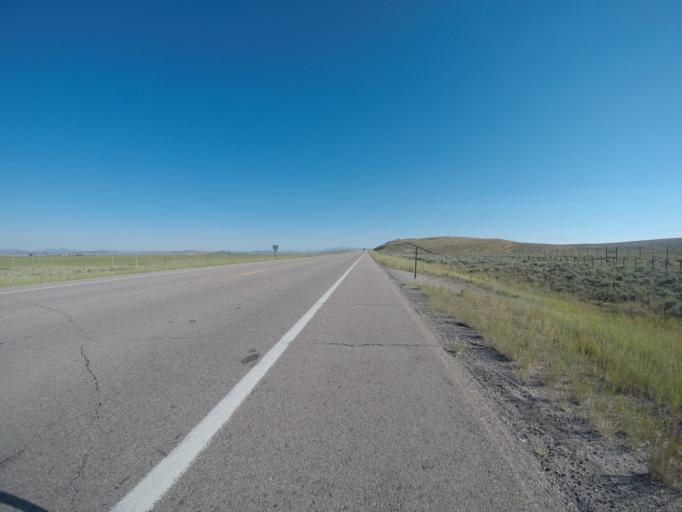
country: US
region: Wyoming
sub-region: Sublette County
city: Pinedale
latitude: 42.9400
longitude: -110.0826
